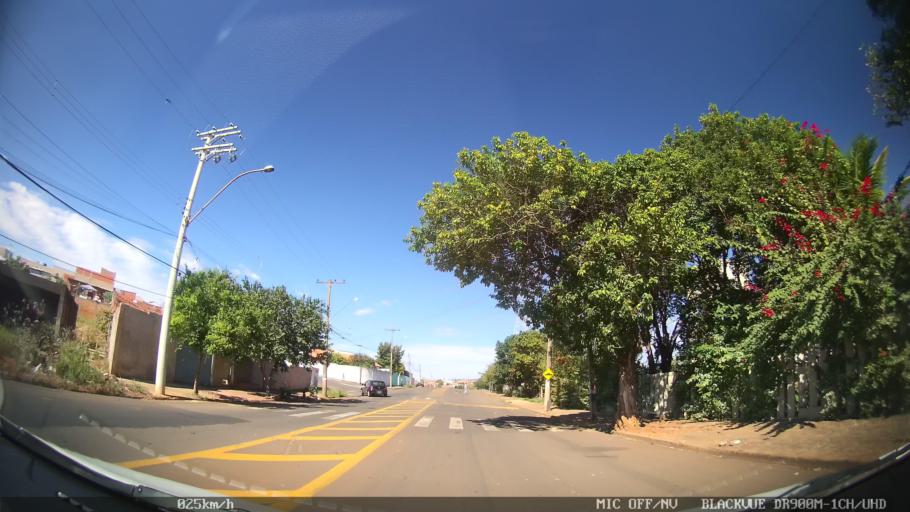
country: BR
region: Sao Paulo
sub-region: Santa Barbara D'Oeste
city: Santa Barbara d'Oeste
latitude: -22.7358
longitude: -47.4036
